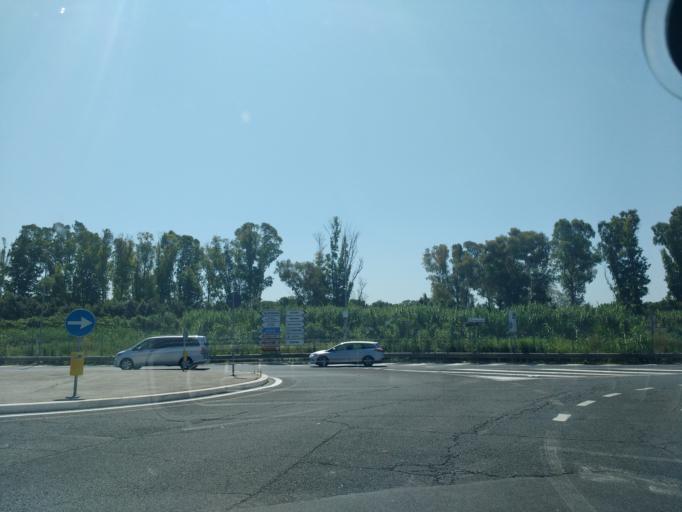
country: IT
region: Latium
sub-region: Citta metropolitana di Roma Capitale
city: Fiumicino-Isola Sacra
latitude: 41.7818
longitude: 12.2541
